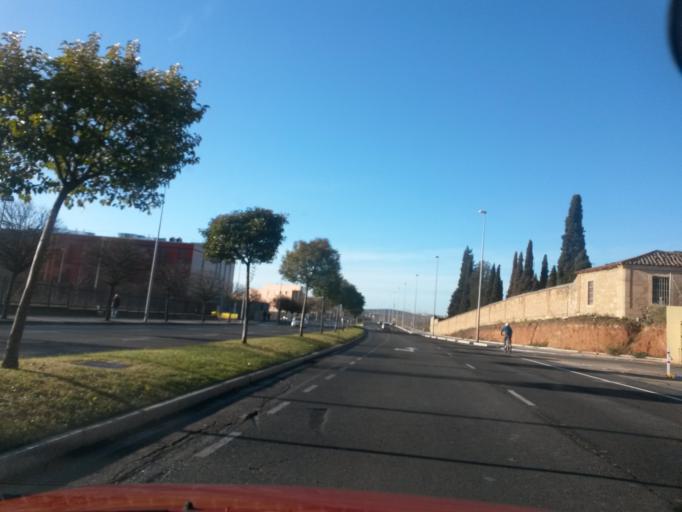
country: ES
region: Castille and Leon
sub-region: Provincia de Salamanca
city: Salamanca
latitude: 40.9711
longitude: -5.6827
